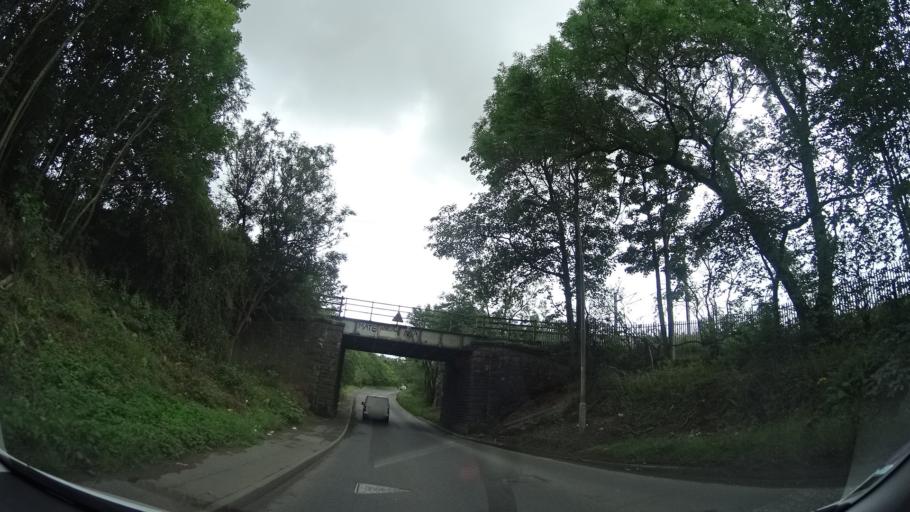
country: GB
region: Scotland
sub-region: Edinburgh
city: Newbridge
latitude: 55.9297
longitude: -3.4156
